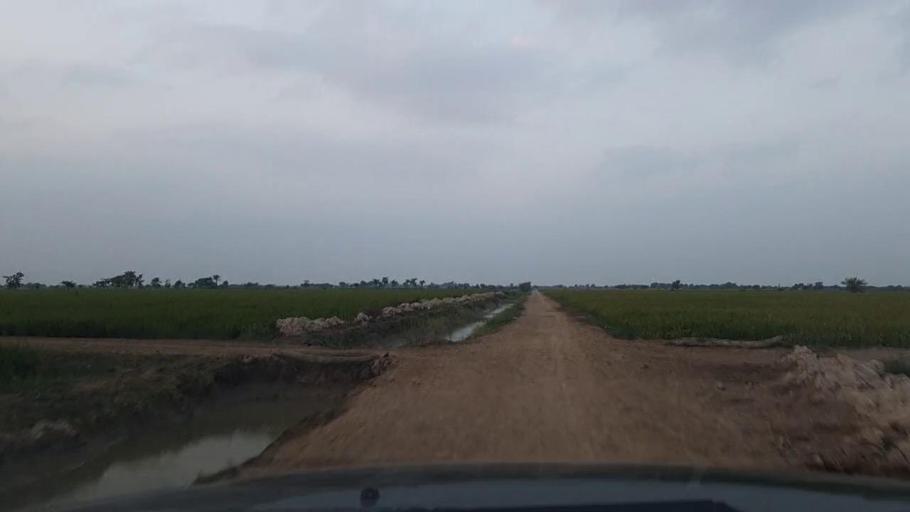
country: PK
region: Sindh
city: Jati
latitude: 24.5033
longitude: 68.3931
